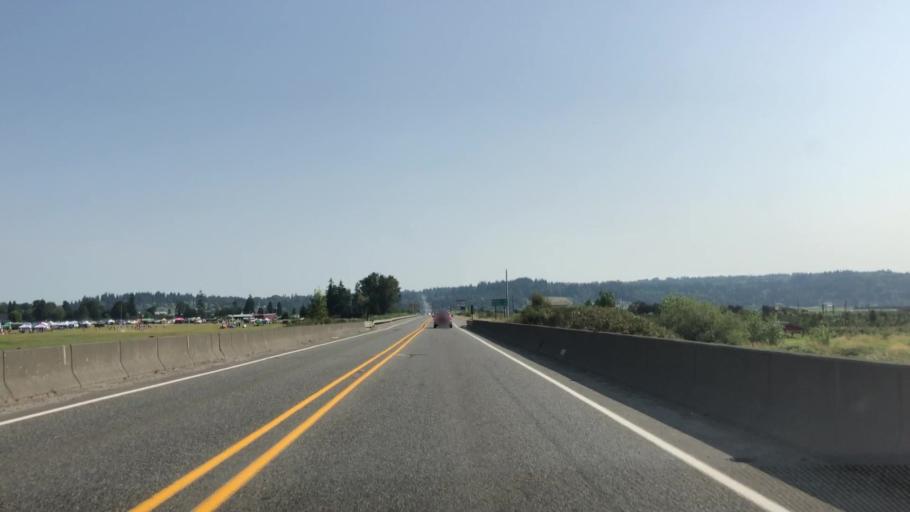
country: US
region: Washington
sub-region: Snohomish County
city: Snohomish
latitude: 47.9061
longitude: -122.1089
